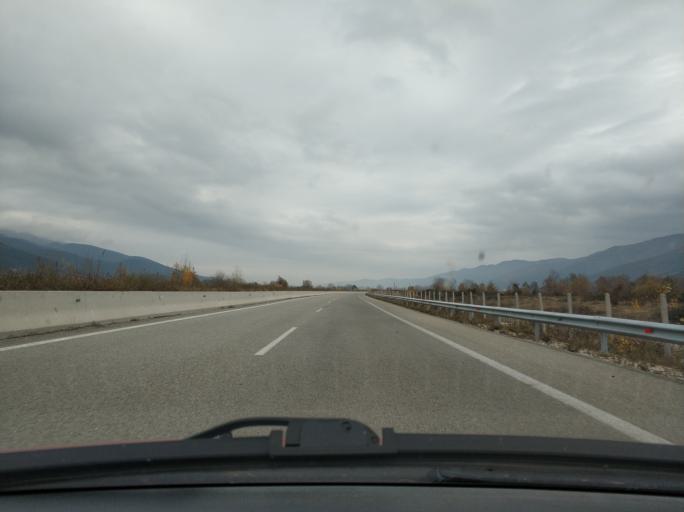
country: GR
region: East Macedonia and Thrace
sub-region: Nomos Kavalas
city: Nikisiani
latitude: 40.8477
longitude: 24.1308
